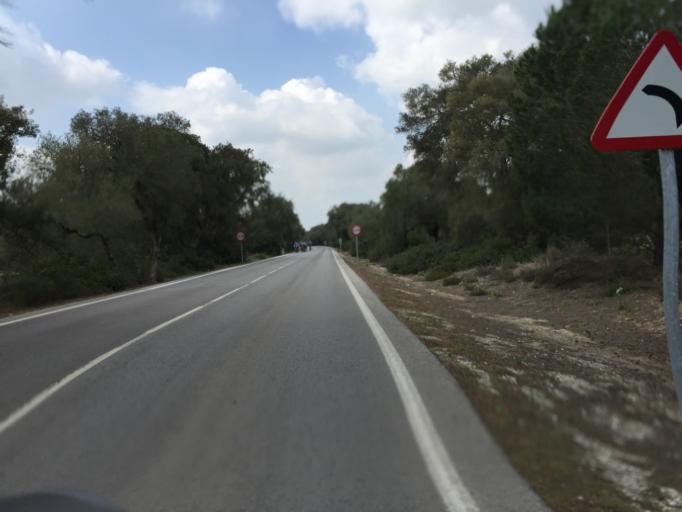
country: ES
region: Andalusia
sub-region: Provincia de Cadiz
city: Vejer de la Frontera
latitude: 36.2966
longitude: -5.9161
